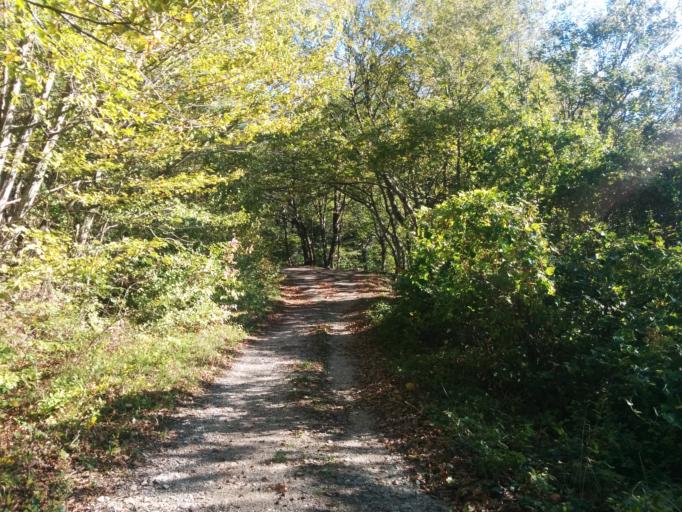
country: RU
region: Krasnodarskiy
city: Agoy
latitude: 44.1502
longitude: 39.0170
